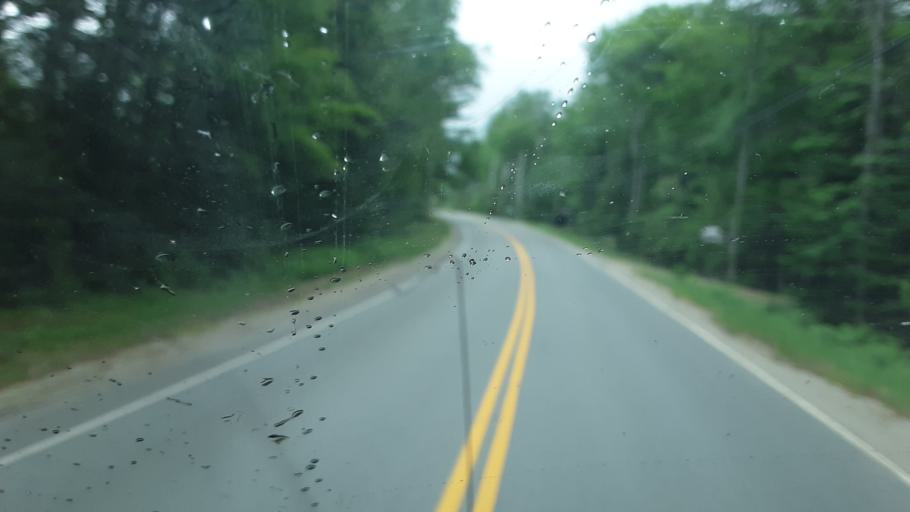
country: US
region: Maine
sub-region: Penobscot County
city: Millinocket
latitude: 45.6845
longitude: -68.7729
